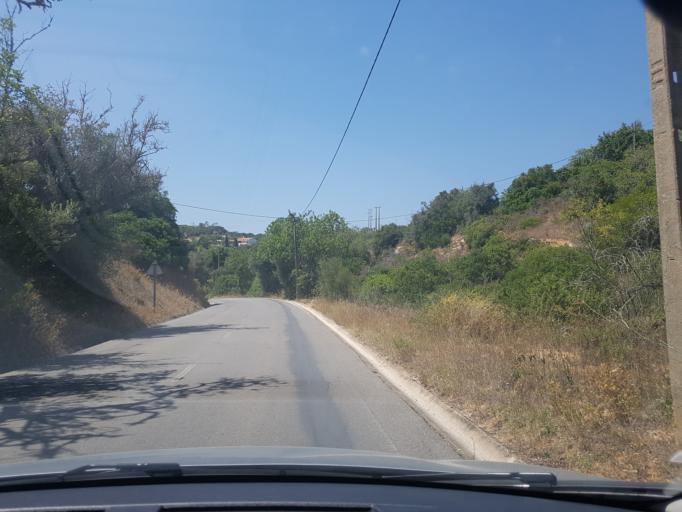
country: PT
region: Faro
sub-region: Lagoa
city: Carvoeiro
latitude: 37.1009
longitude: -8.4264
